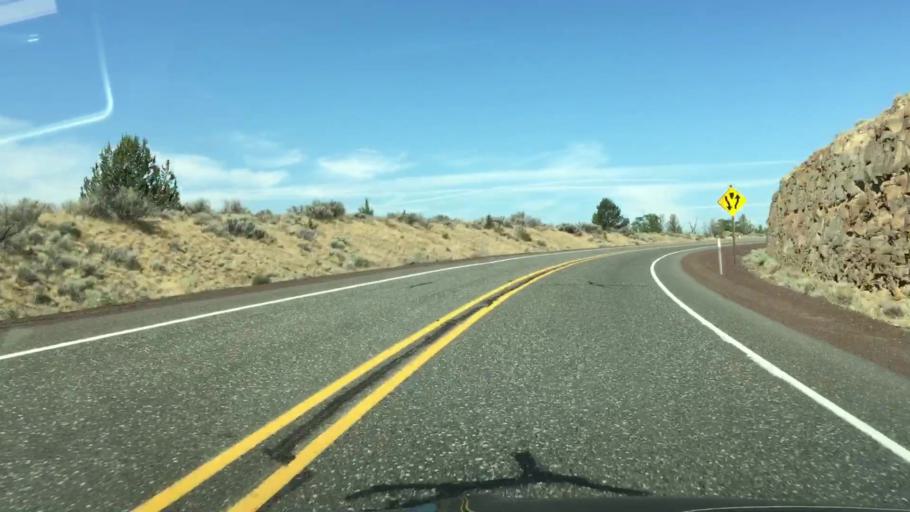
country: US
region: Oregon
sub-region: Jefferson County
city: Warm Springs
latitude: 45.1673
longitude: -121.1165
